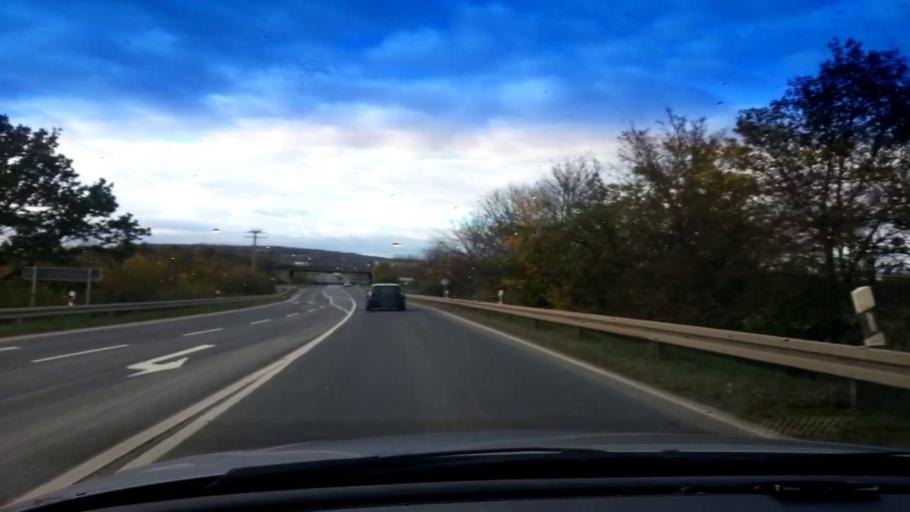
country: DE
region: Bavaria
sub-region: Upper Franconia
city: Breitengussbach
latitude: 49.9771
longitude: 10.8883
